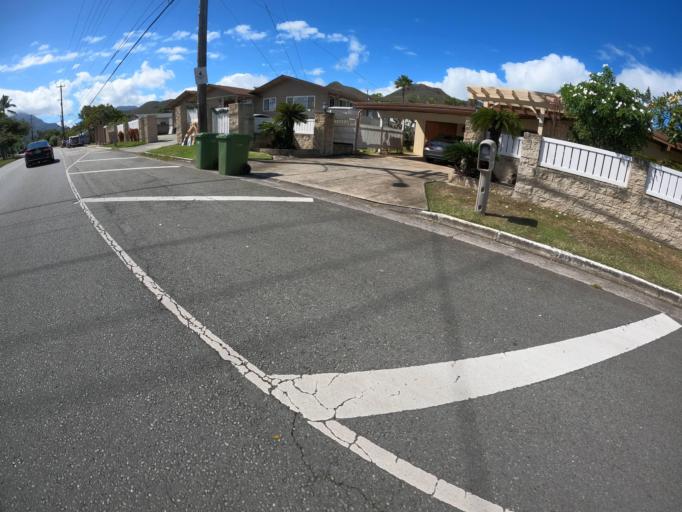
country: US
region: Hawaii
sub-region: Honolulu County
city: Kailua
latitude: 21.4210
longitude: -157.7485
